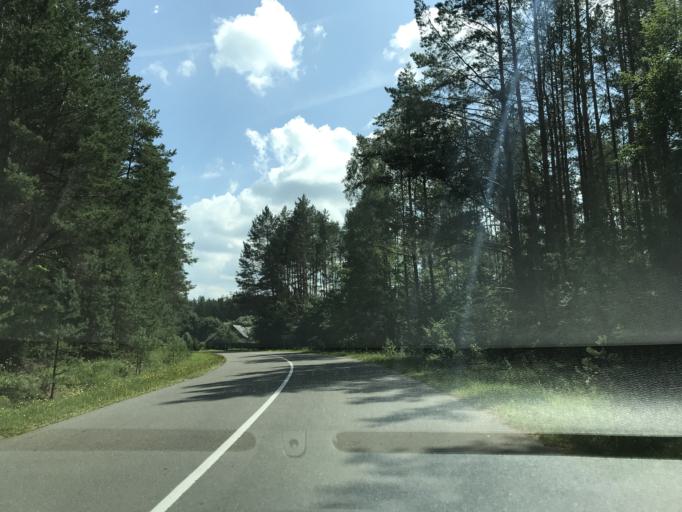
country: BY
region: Minsk
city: Rakaw
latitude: 53.9966
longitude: 26.9874
